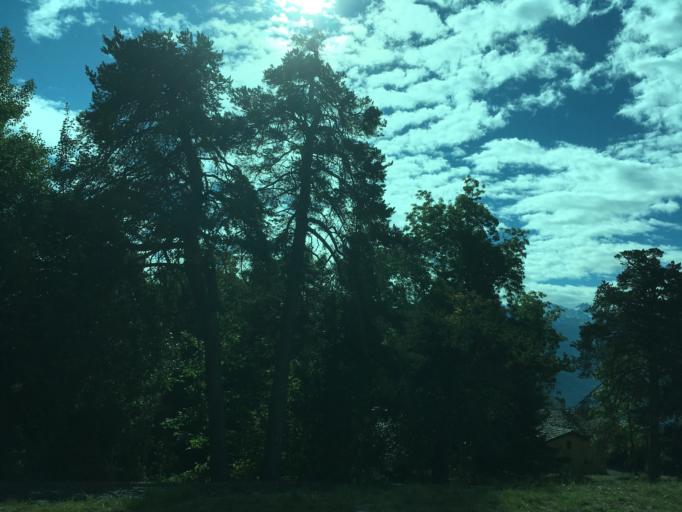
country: CH
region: Valais
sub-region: Sierre District
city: Montana
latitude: 46.2984
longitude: 7.4854
